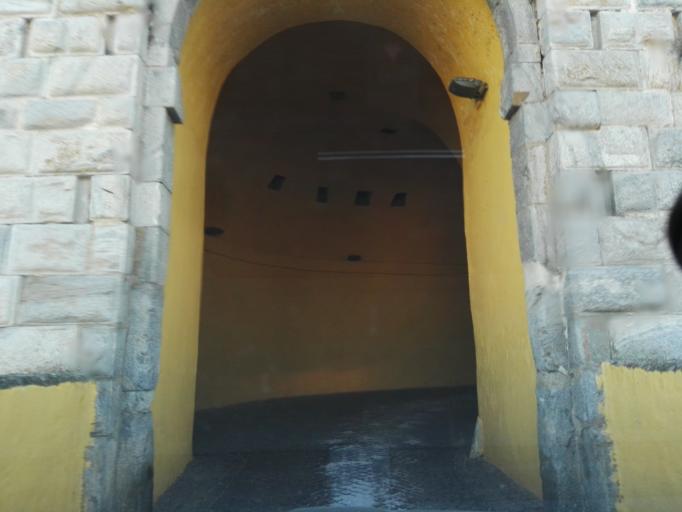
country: PT
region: Portalegre
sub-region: Elvas
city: Elvas
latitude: 38.8825
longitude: -7.1600
